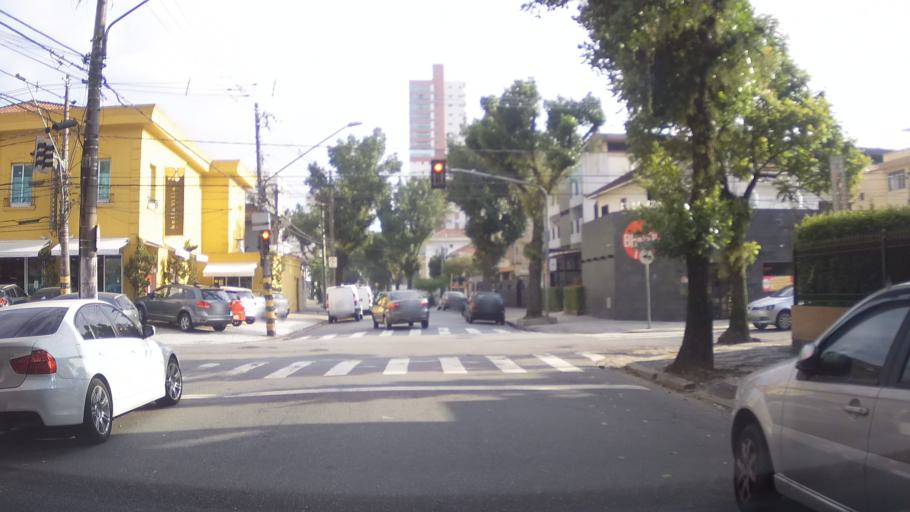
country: BR
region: Sao Paulo
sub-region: Santos
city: Santos
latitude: -23.9612
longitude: -46.3249
